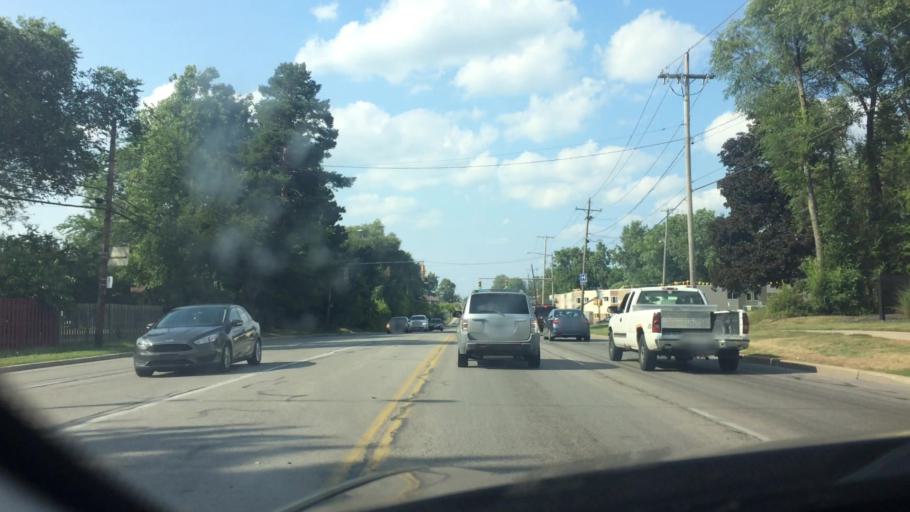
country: US
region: Ohio
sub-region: Lucas County
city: Ottawa Hills
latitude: 41.6170
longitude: -83.6257
